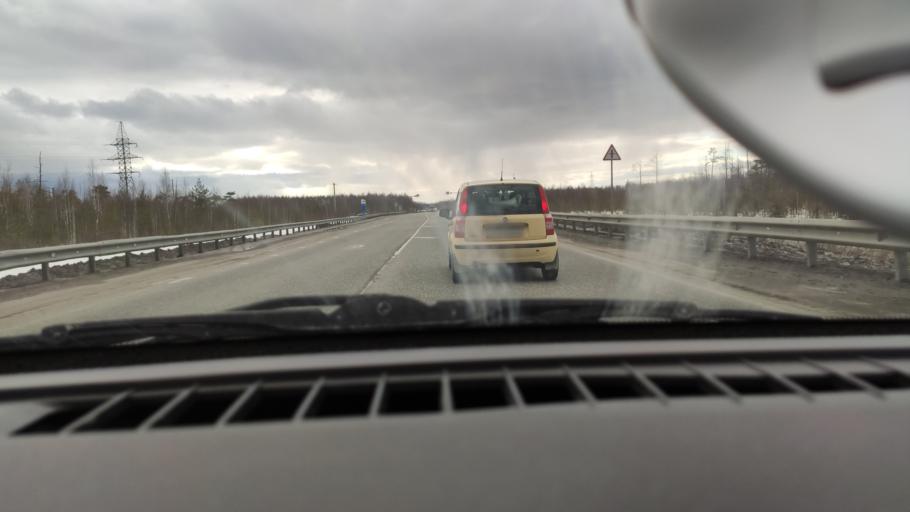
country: RU
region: Perm
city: Krasnokamsk
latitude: 58.1030
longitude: 55.7572
